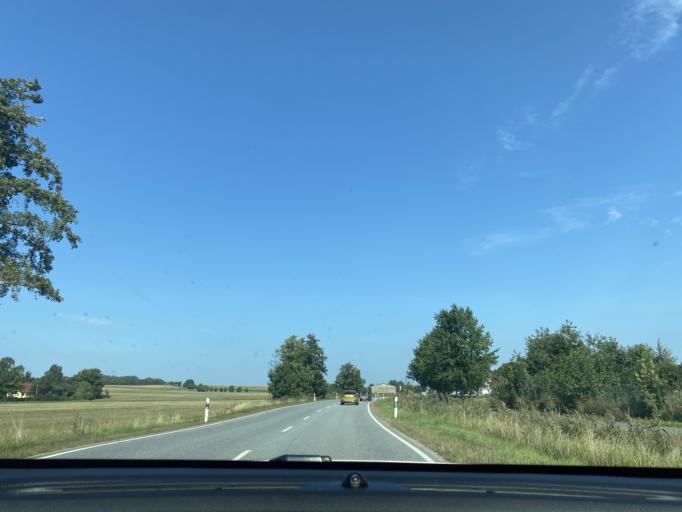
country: DE
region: Saxony
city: Quitzdorf
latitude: 51.2186
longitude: 14.7721
